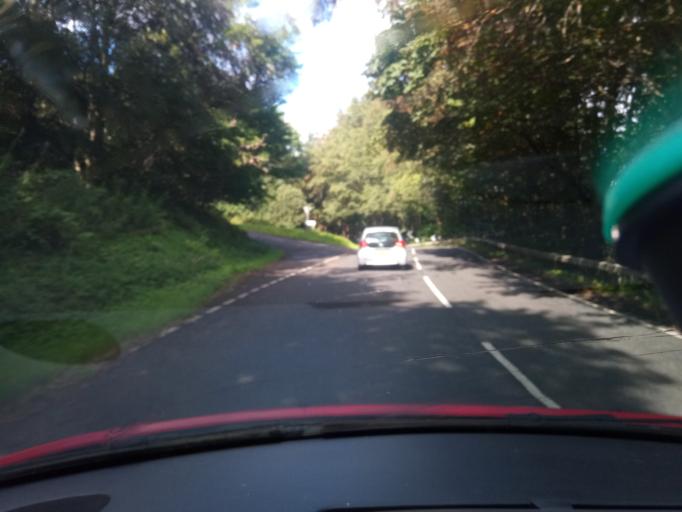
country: GB
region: Scotland
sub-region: The Scottish Borders
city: Jedburgh
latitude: 55.5719
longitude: -2.5410
